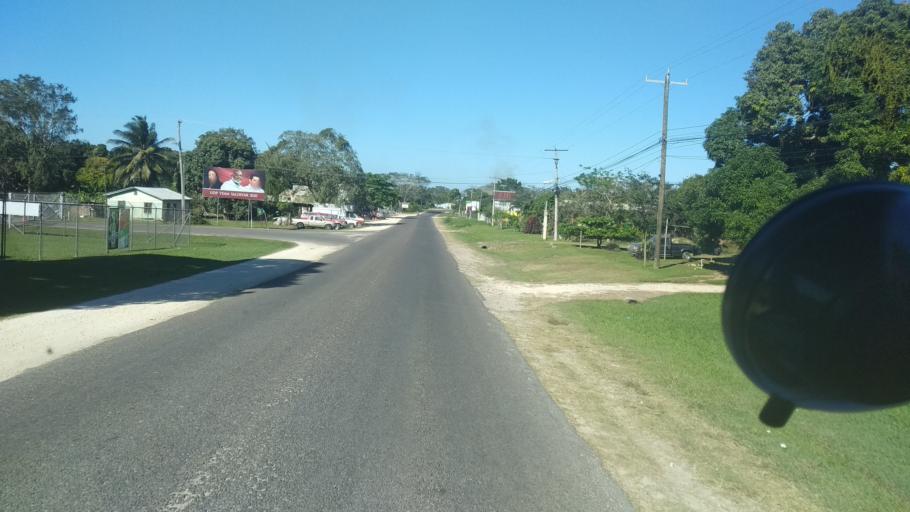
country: BZ
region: Cayo
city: San Ignacio
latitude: 17.1746
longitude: -89.0484
